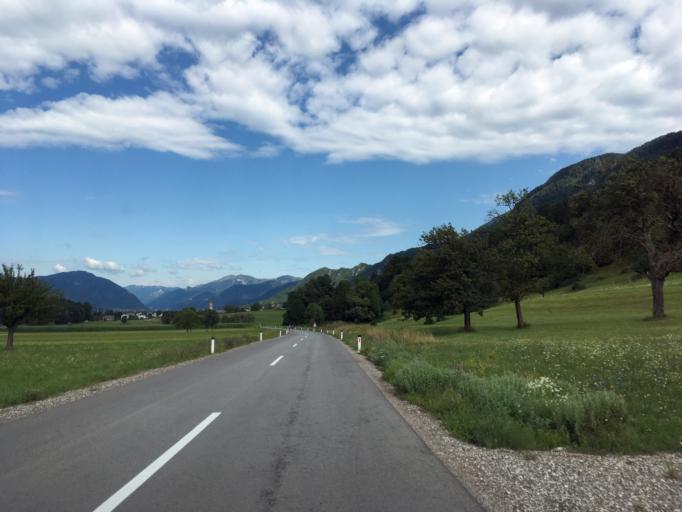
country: SI
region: Radovljica
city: Lesce
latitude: 46.3771
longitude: 14.1863
